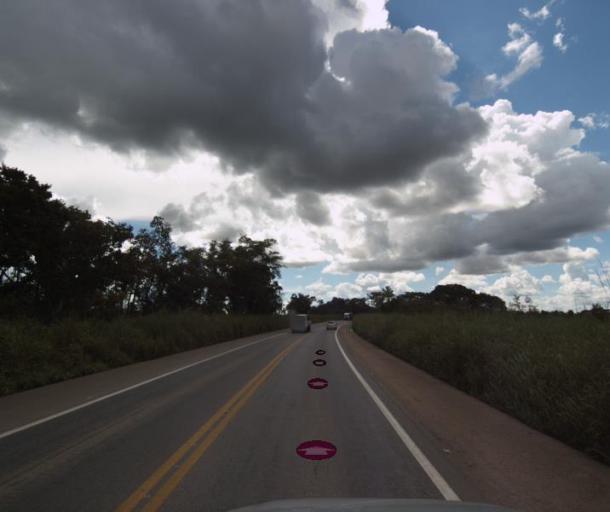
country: BR
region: Goias
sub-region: Porangatu
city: Porangatu
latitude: -13.5501
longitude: -49.0992
